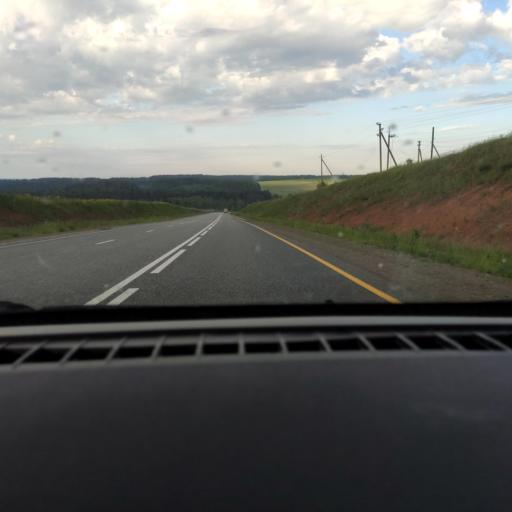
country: RU
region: Udmurtiya
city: Votkinsk
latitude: 57.2380
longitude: 54.1984
